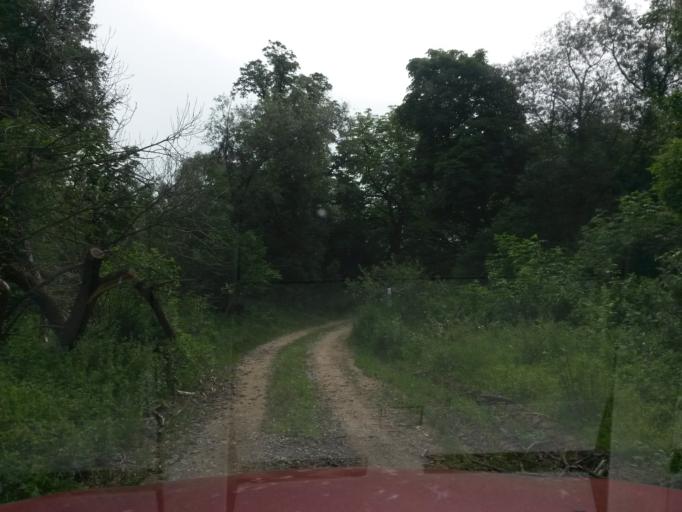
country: SK
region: Kosicky
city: Moldava nad Bodvou
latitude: 48.6712
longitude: 21.1216
